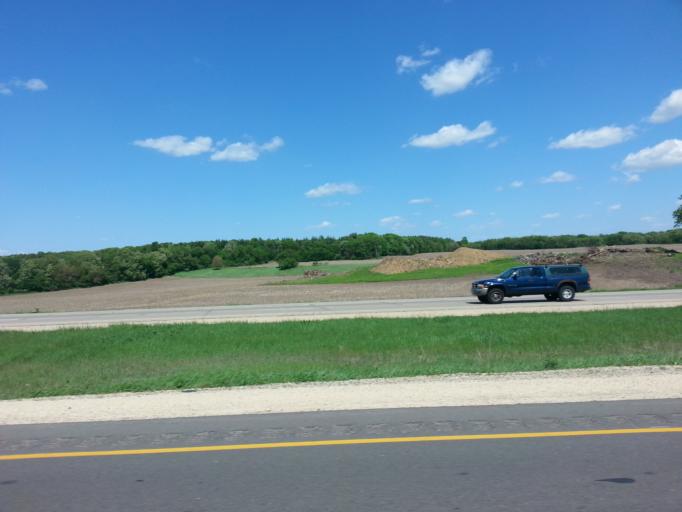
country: US
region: Wisconsin
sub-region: Rock County
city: Janesville
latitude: 42.7356
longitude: -89.0040
